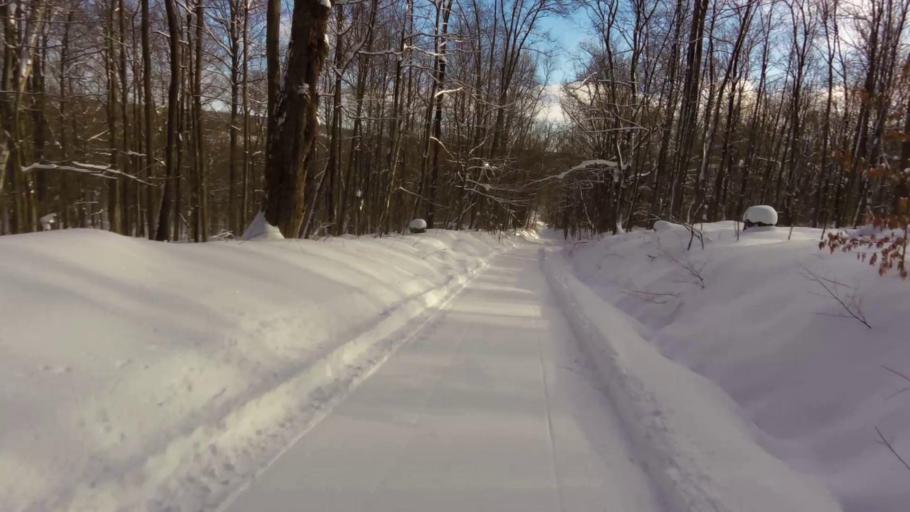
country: US
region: New York
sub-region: Chautauqua County
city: Falconer
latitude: 42.2441
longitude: -79.1496
